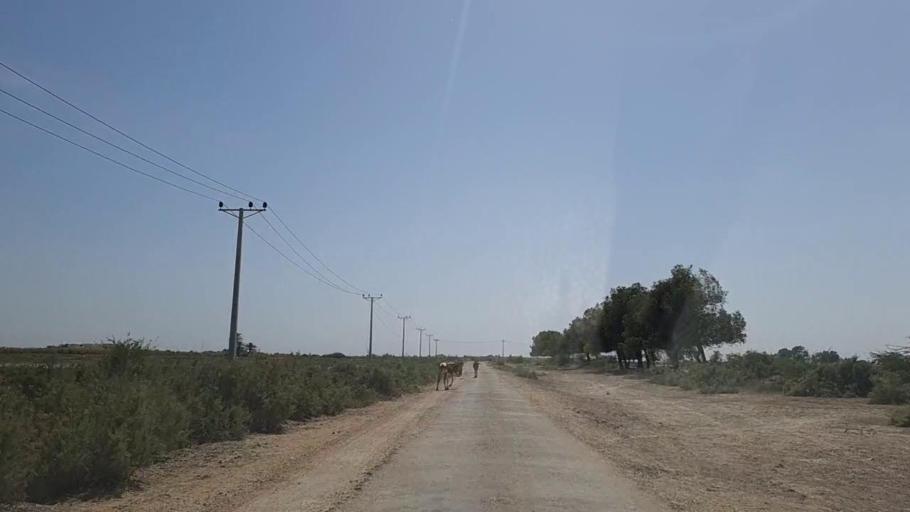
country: PK
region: Sindh
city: Gharo
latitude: 24.7704
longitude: 67.7525
